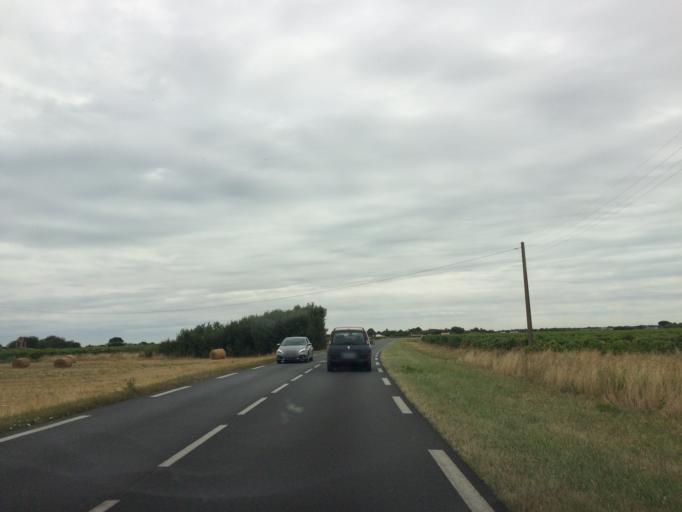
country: FR
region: Poitou-Charentes
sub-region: Departement de la Charente-Maritime
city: Le Bois-Plage-en-Re
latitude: 46.2006
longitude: -1.3971
